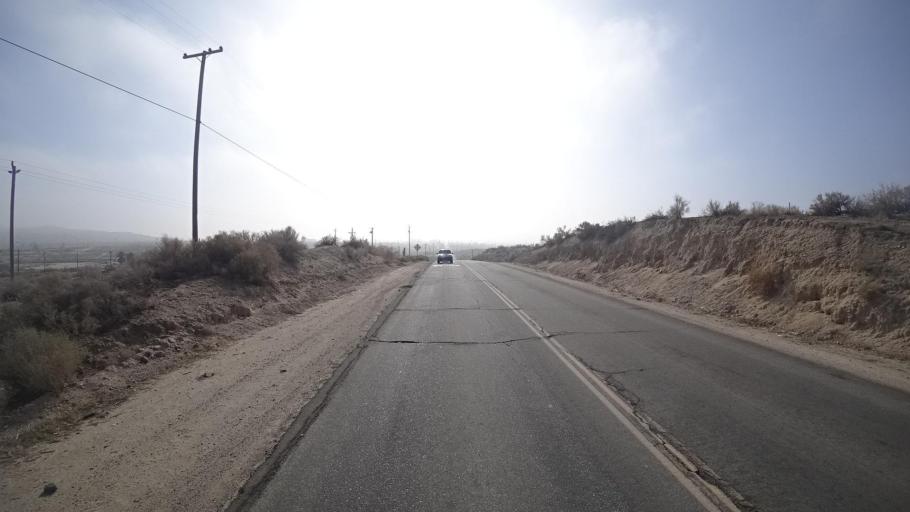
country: US
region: California
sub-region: Kern County
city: Ford City
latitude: 35.1793
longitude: -119.4657
